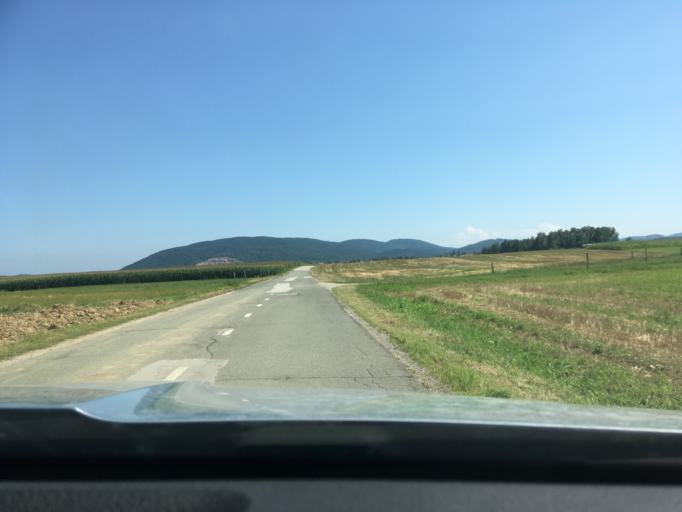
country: SI
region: Metlika
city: Metlika
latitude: 45.5858
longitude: 15.2819
